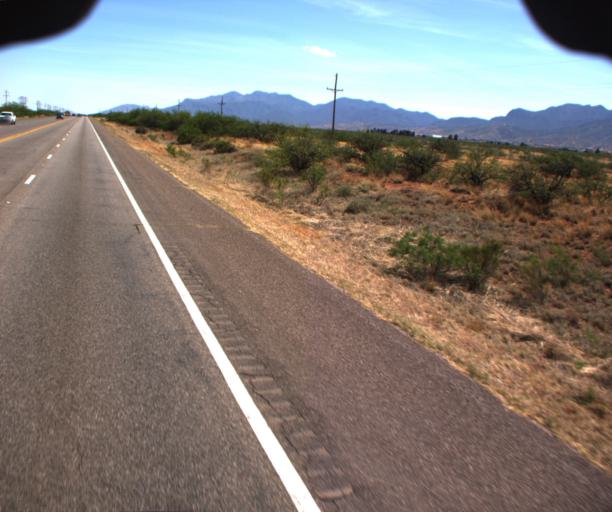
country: US
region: Arizona
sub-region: Cochise County
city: Huachuca City
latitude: 31.6033
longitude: -110.3288
